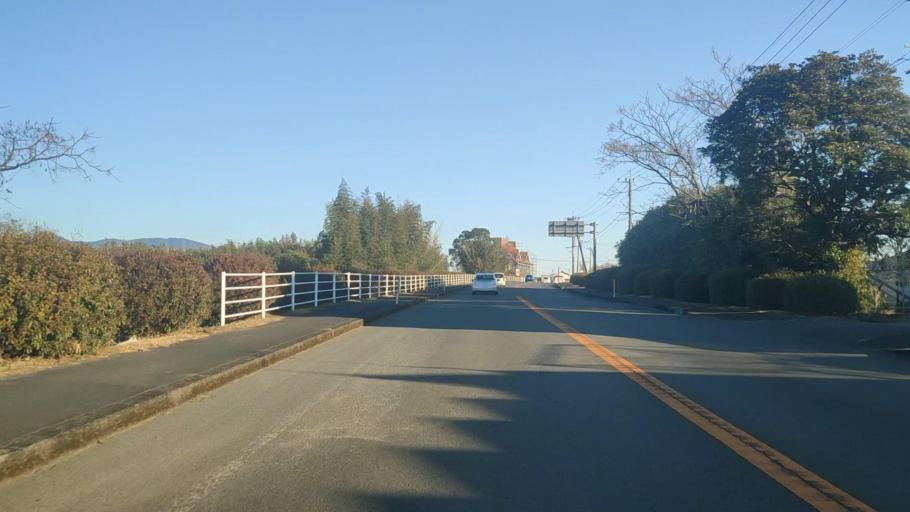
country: JP
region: Miyazaki
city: Takanabe
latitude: 32.1935
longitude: 131.5244
